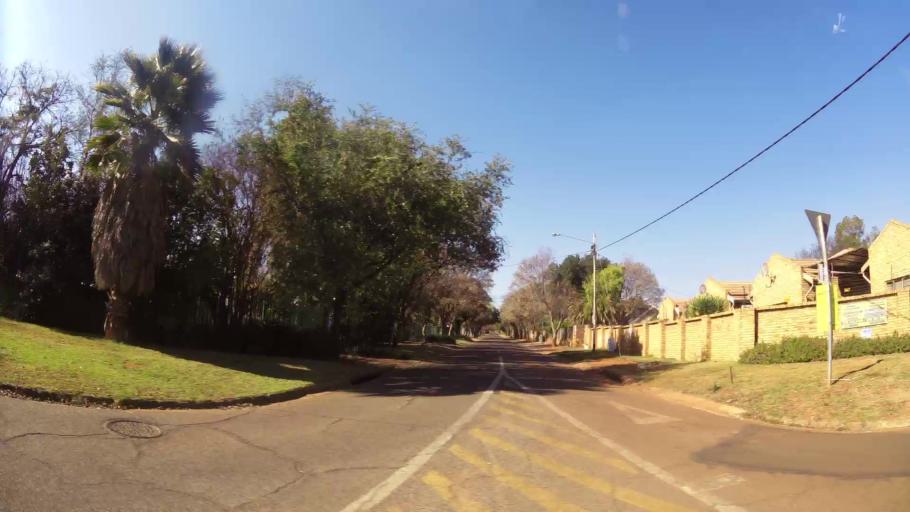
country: ZA
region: Gauteng
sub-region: City of Tshwane Metropolitan Municipality
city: Centurion
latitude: -25.8335
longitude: 28.1718
